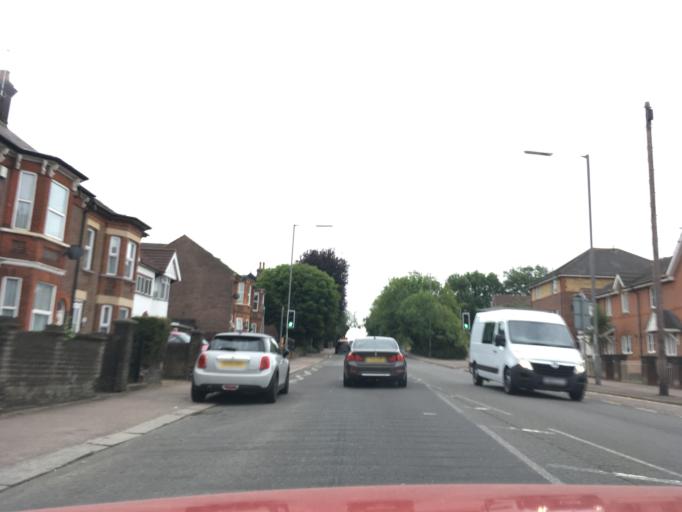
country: GB
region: England
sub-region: Central Bedfordshire
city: Dunstable
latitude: 51.8810
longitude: -0.5133
